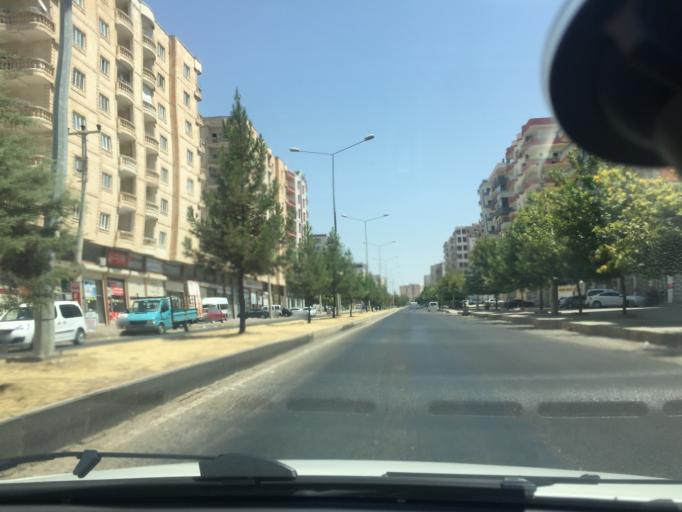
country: TR
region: Mardin
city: Midyat
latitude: 37.4334
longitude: 41.3322
